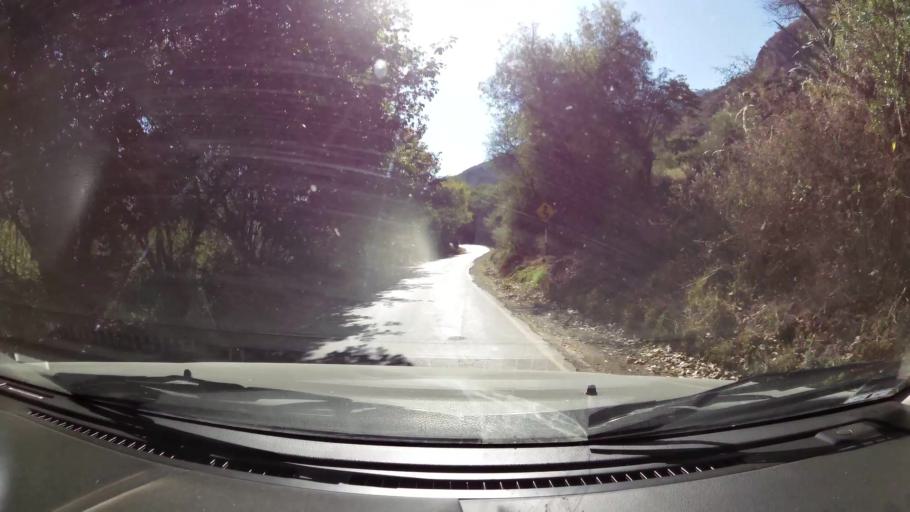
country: PE
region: Huancavelica
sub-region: Provincia de Acobamba
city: Pomacocha
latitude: -12.7694
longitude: -74.5005
